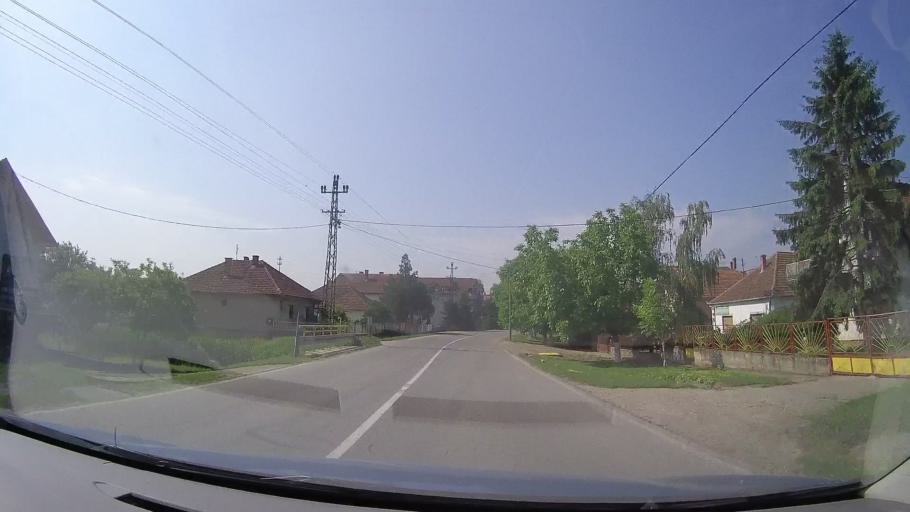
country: RS
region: Autonomna Pokrajina Vojvodina
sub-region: Srednjebanatski Okrug
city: Secanj
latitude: 45.3679
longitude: 20.7769
